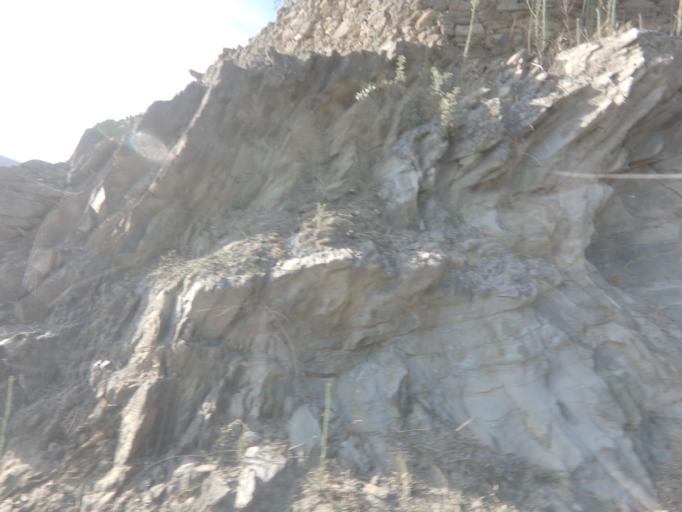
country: PT
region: Vila Real
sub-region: Sabrosa
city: Vilela
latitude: 41.2075
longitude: -7.5411
